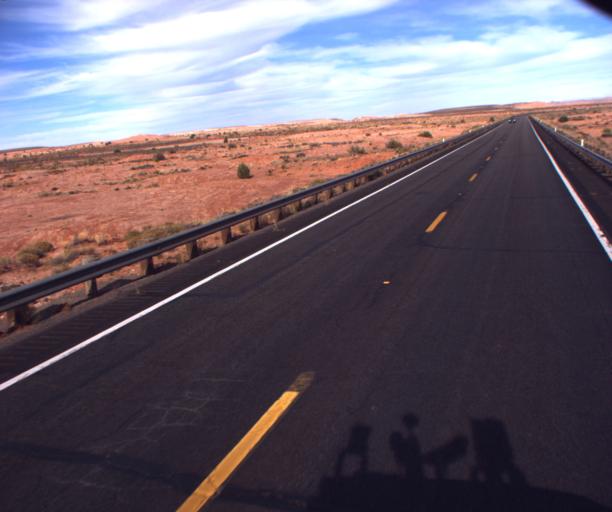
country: US
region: Arizona
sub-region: Navajo County
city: Kayenta
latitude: 36.9437
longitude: -109.7263
